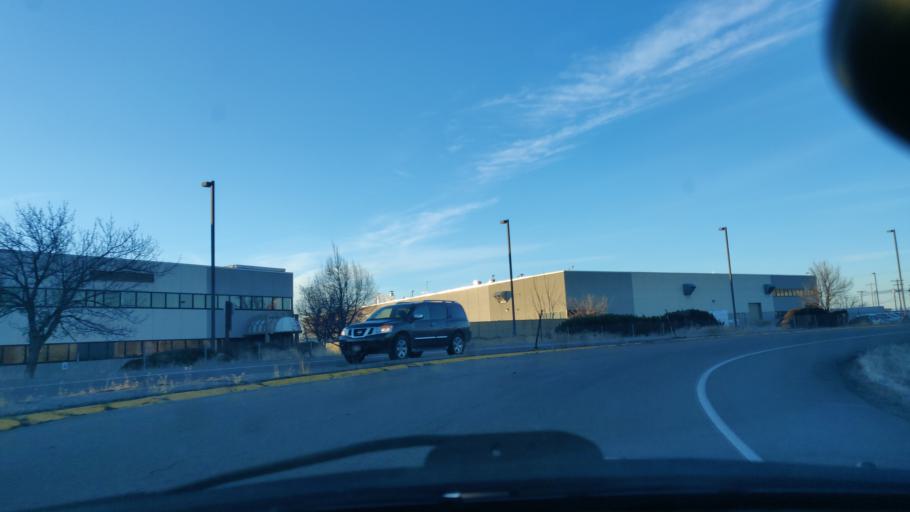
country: US
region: Idaho
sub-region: Ada County
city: Boise
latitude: 43.5739
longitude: -116.1947
